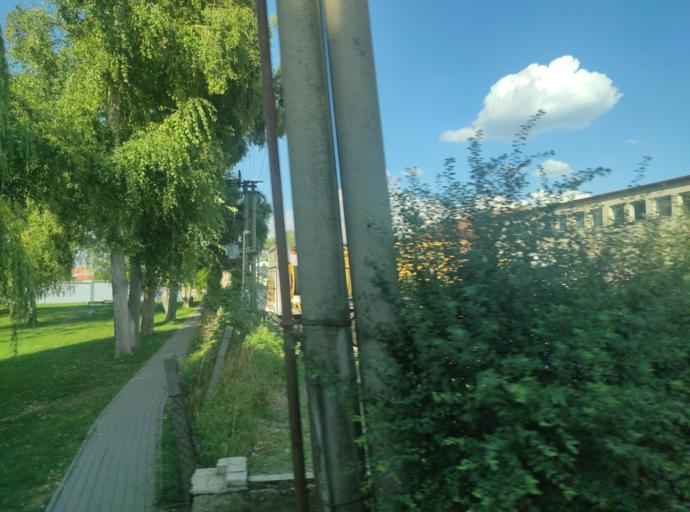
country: CZ
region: South Moravian
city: Vinicne Sumice
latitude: 49.1811
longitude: 16.8467
